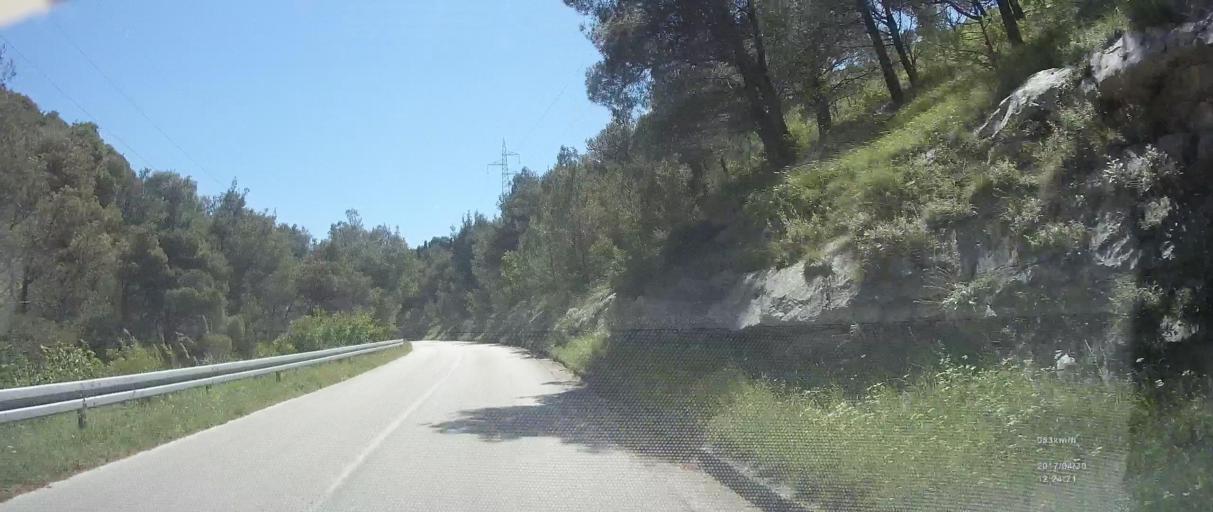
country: HR
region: Splitsko-Dalmatinska
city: Zrnovnica
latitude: 43.5121
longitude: 16.5851
